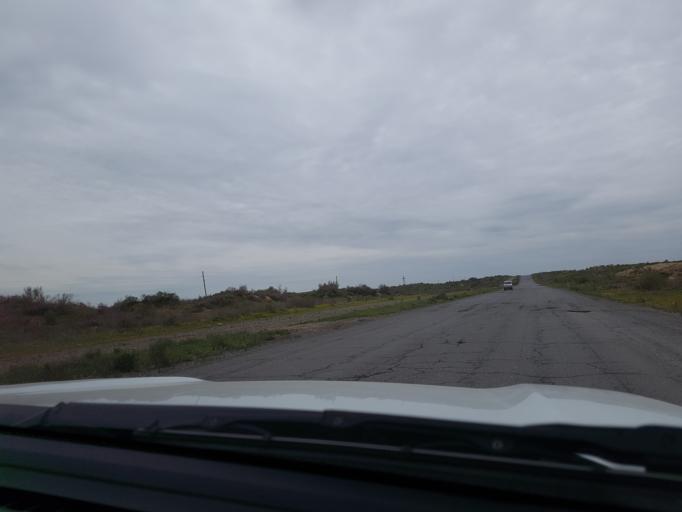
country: TM
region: Mary
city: Bayramaly
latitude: 37.8913
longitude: 62.6155
